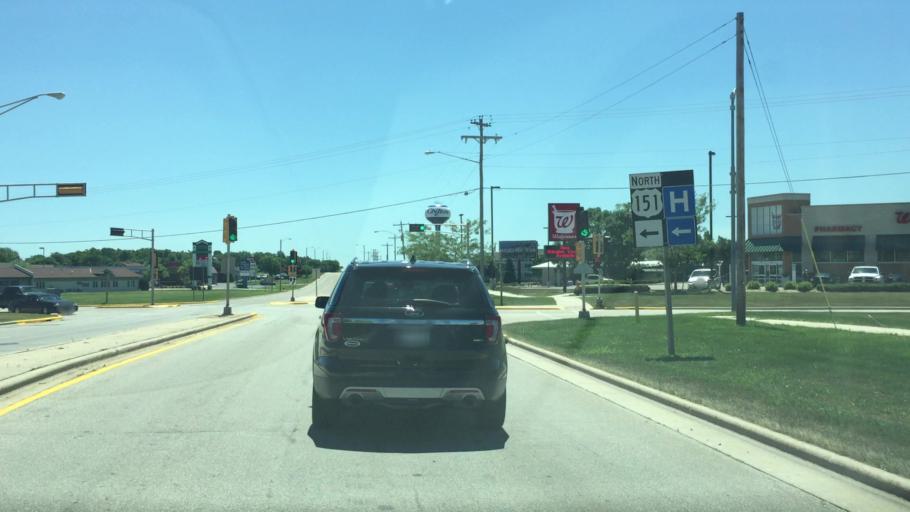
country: US
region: Wisconsin
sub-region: Calumet County
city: Chilton
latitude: 44.0229
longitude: -88.1556
